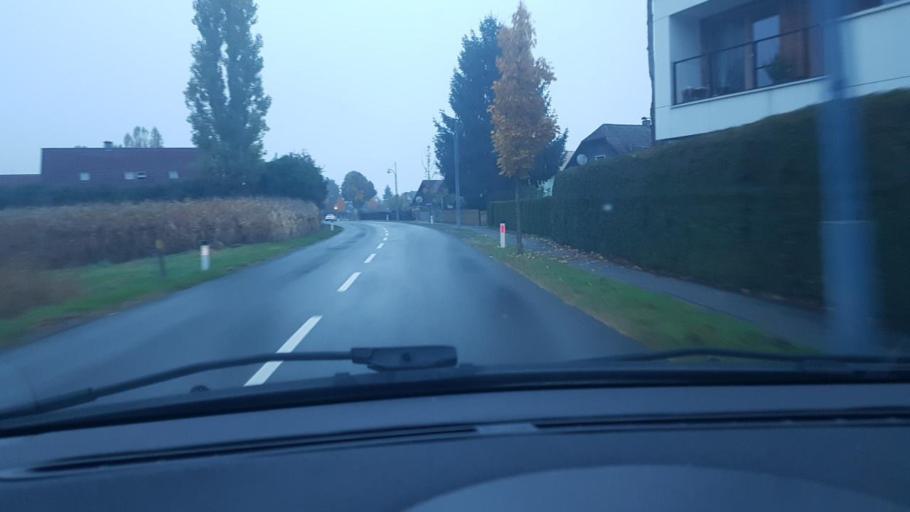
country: AT
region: Styria
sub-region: Politischer Bezirk Leibnitz
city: Obervogau
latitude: 46.7378
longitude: 15.5820
